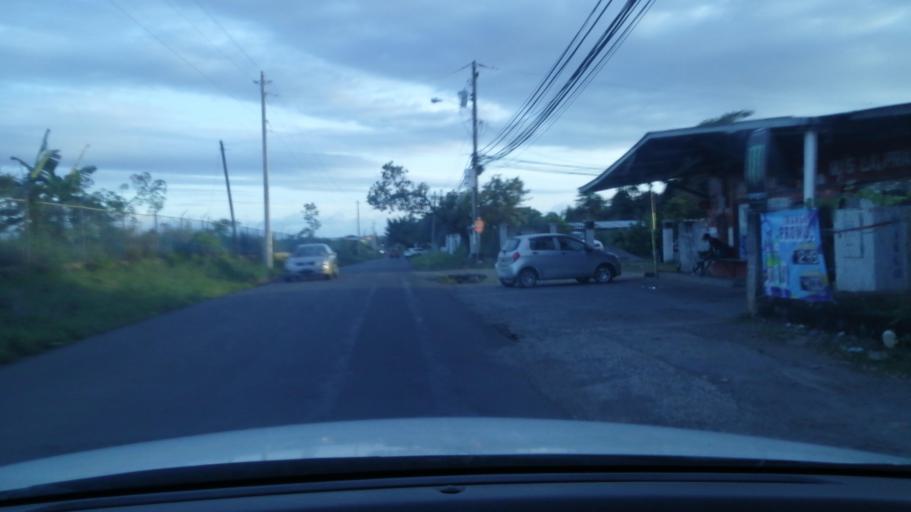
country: PA
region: Chiriqui
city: David
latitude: 8.4072
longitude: -82.4346
